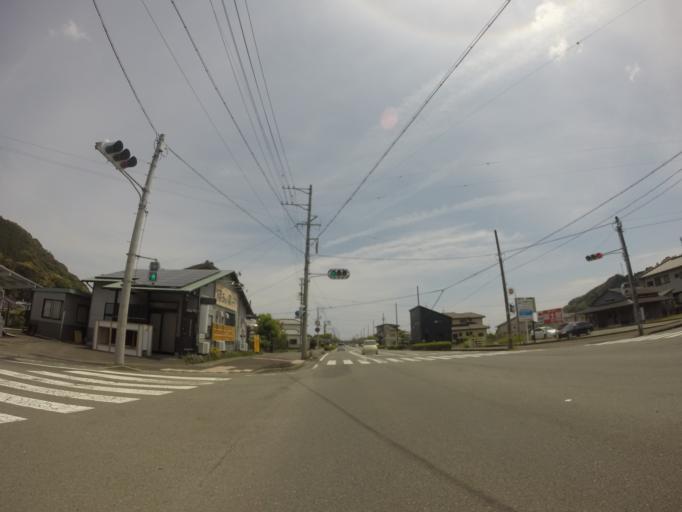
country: JP
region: Shizuoka
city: Fujieda
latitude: 34.8929
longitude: 138.2511
